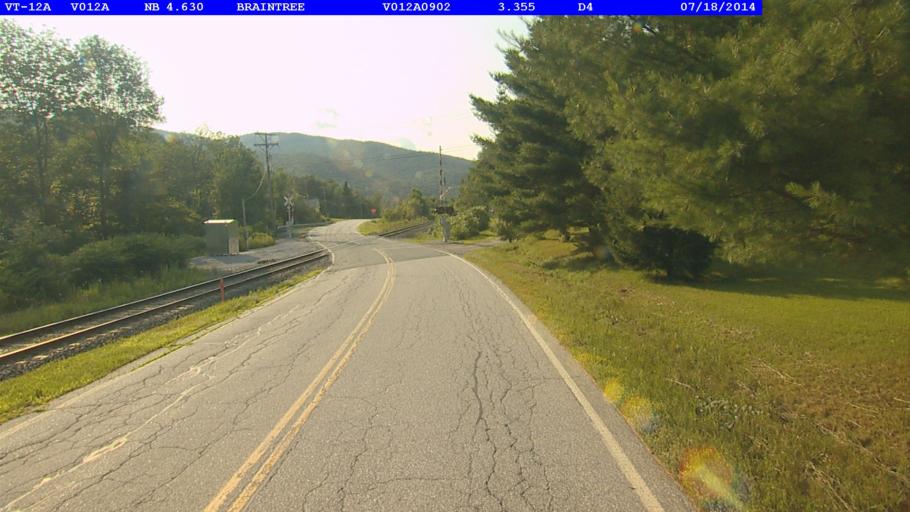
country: US
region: Vermont
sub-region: Orange County
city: Randolph
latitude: 43.9602
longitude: -72.7339
